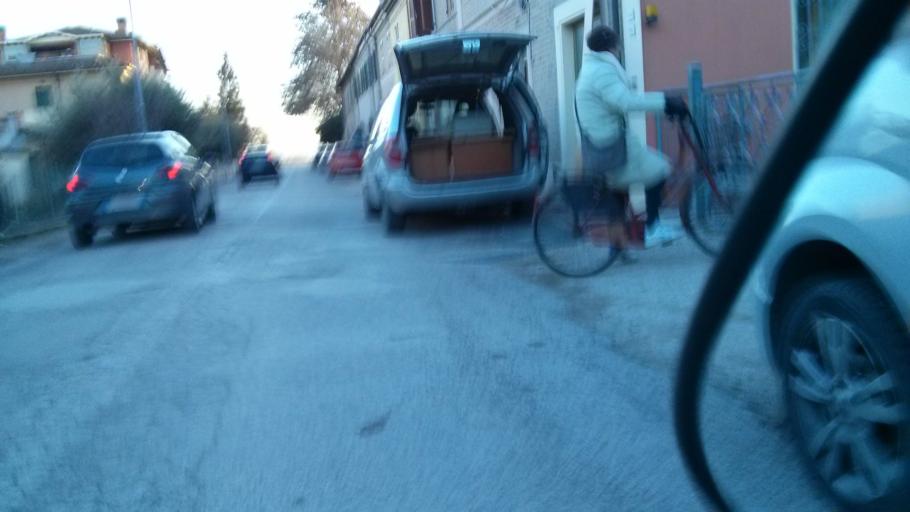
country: IT
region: The Marches
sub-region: Provincia di Pesaro e Urbino
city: Fano
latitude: 43.8306
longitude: 13.0235
